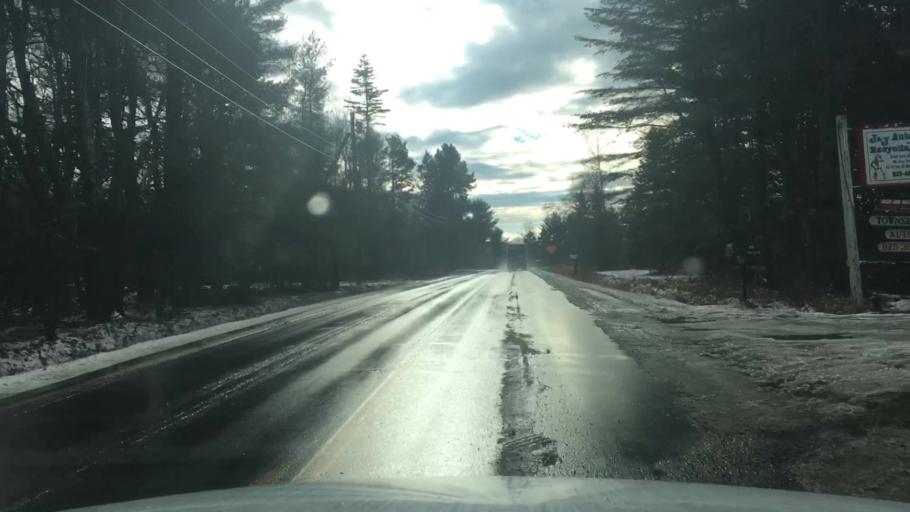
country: US
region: Maine
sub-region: Penobscot County
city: Brewer
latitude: 44.7458
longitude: -68.7664
